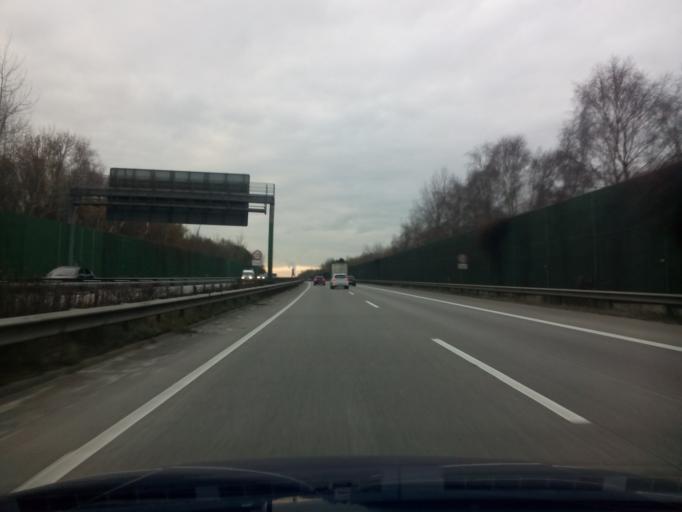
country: DE
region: Lower Saxony
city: Langen
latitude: 53.5751
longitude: 8.6200
